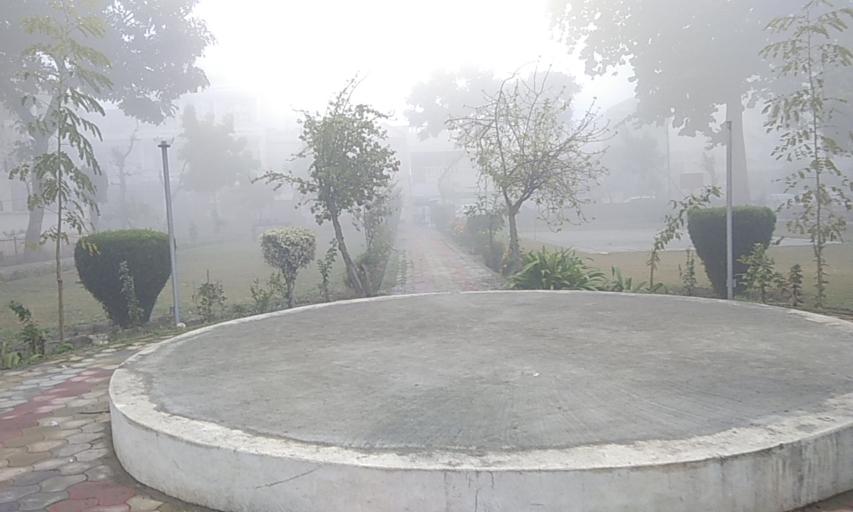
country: IN
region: Punjab
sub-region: Amritsar
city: Amritsar
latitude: 31.6444
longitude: 74.8662
